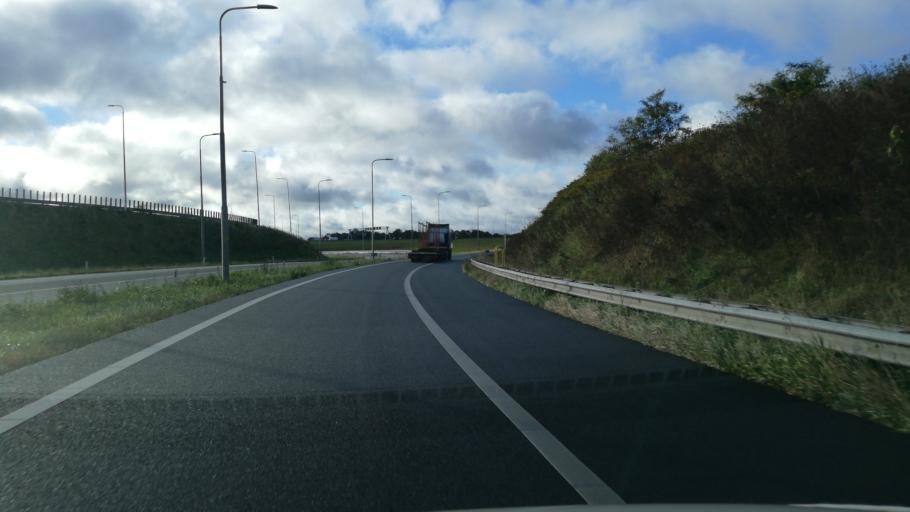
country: NL
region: Gelderland
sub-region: Gemeente Apeldoorn
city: Apeldoorn
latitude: 52.1909
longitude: 6.0200
